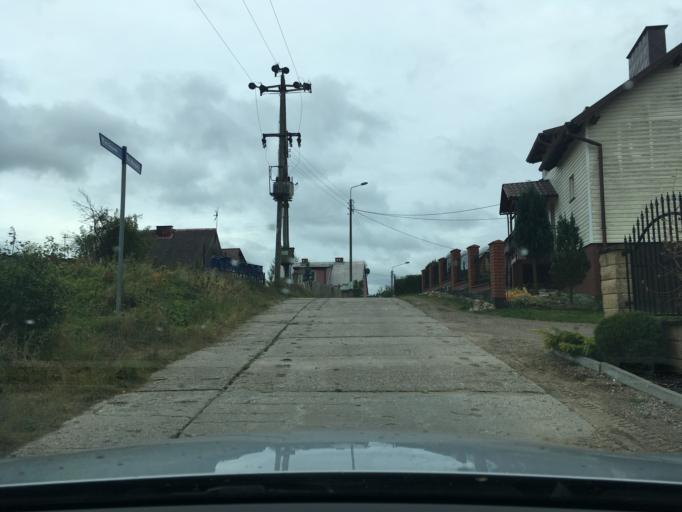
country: PL
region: Pomeranian Voivodeship
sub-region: Powiat koscierski
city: Koscierzyna
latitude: 54.1010
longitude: 17.9731
